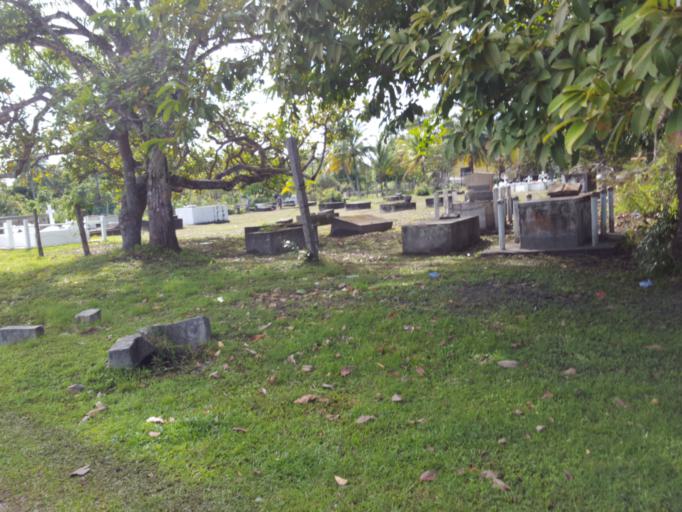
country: BZ
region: Belize
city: Belize City
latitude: 17.5680
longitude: -88.4028
